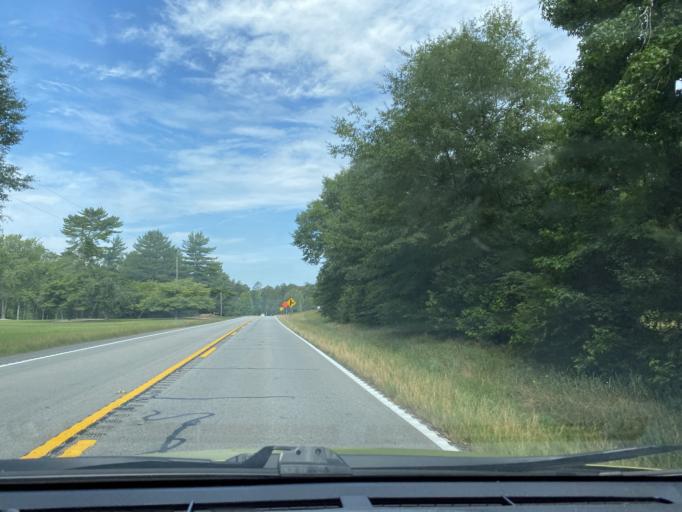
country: US
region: Georgia
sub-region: Coweta County
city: East Newnan
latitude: 33.3002
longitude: -84.6798
